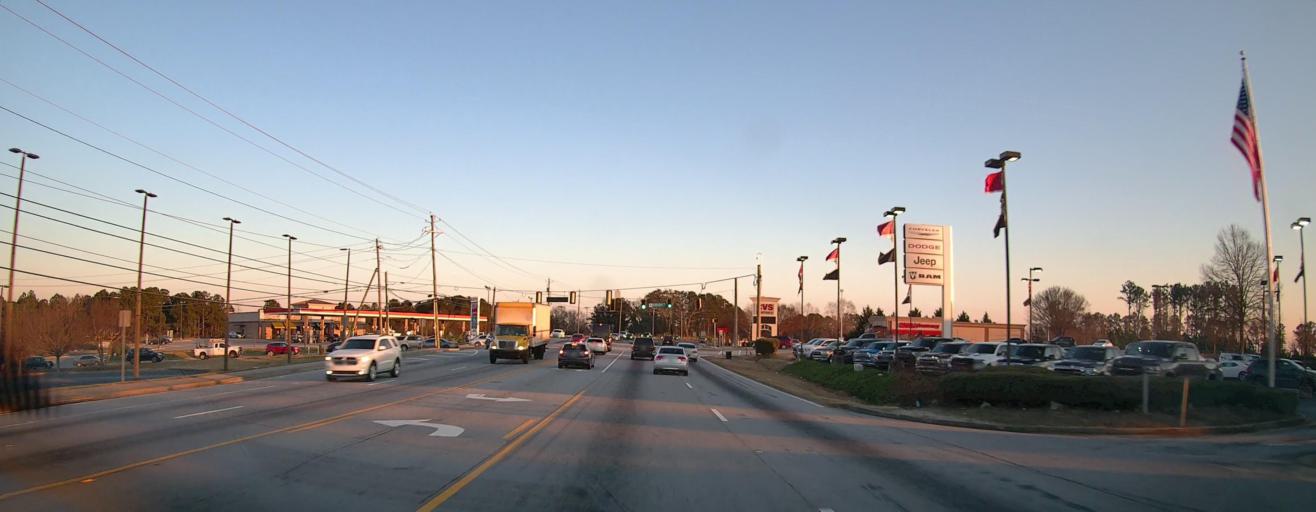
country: US
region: Georgia
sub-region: Fulton County
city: Union City
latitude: 33.5636
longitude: -84.5189
